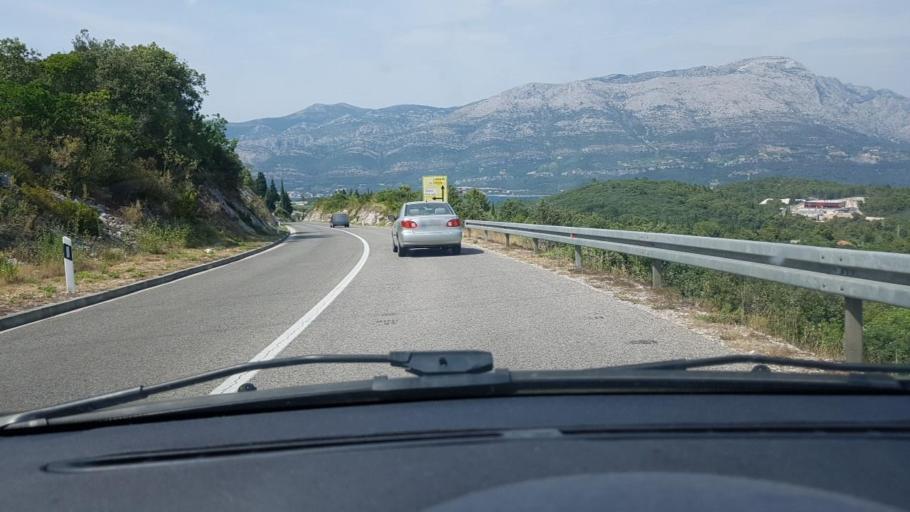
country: HR
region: Dubrovacko-Neretvanska
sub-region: Grad Korcula
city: Zrnovo
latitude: 42.9462
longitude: 17.1203
